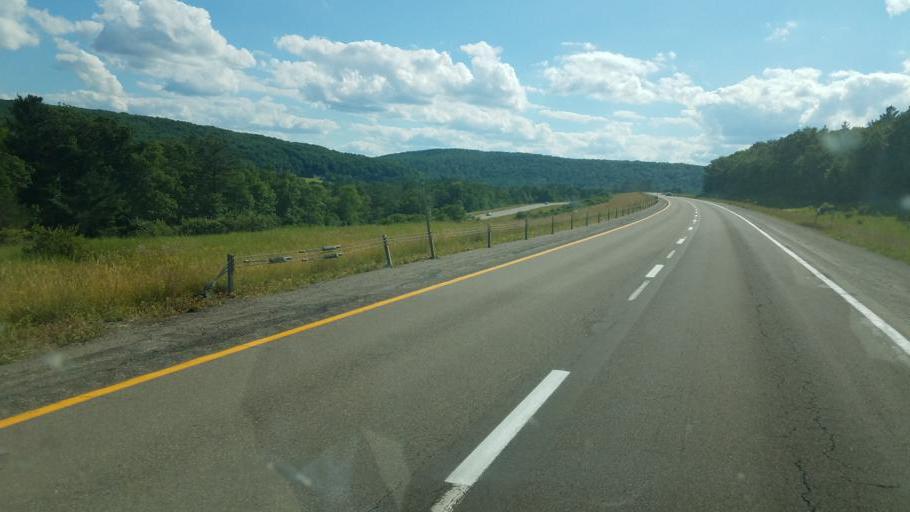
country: US
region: New York
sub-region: Allegany County
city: Belmont
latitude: 42.3008
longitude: -77.9226
